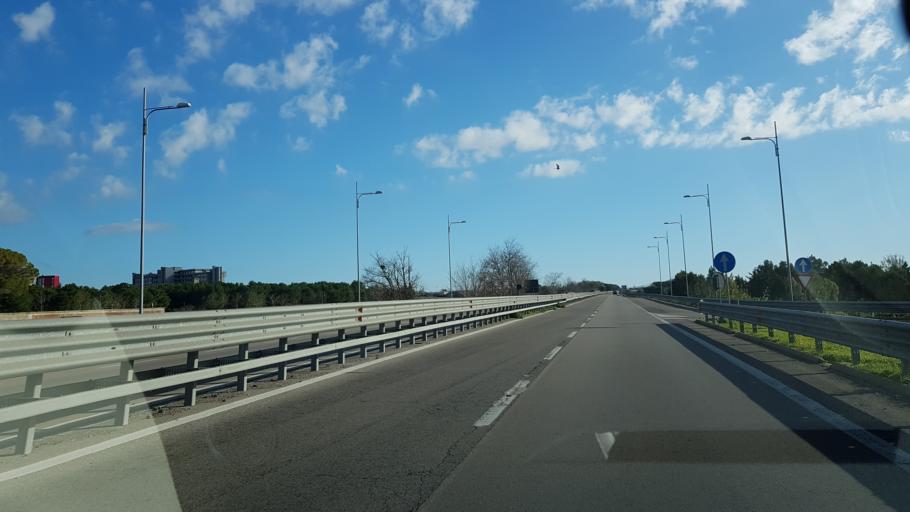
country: IT
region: Apulia
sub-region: Provincia di Lecce
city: Castromediano
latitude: 40.3261
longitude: 18.1547
